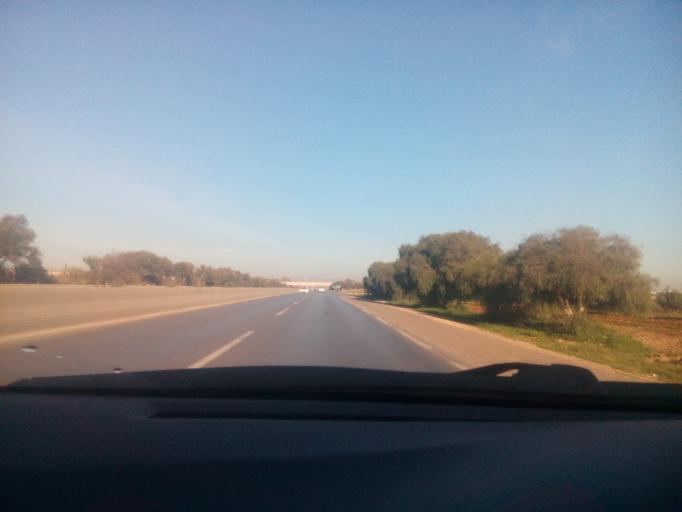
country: DZ
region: Oran
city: Bir el Djir
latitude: 35.7463
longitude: -0.4949
